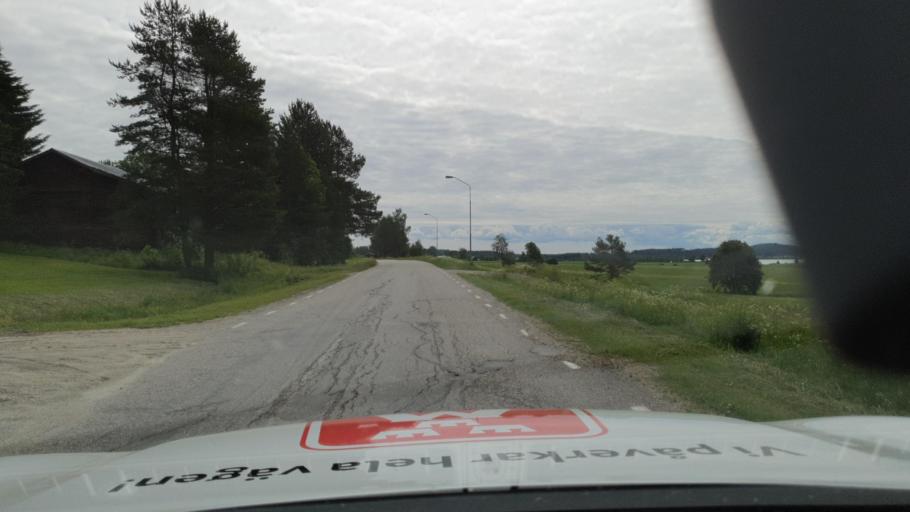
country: SE
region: Vaesterbotten
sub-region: Skelleftea Kommun
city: Forsbacka
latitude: 64.6261
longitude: 20.4869
